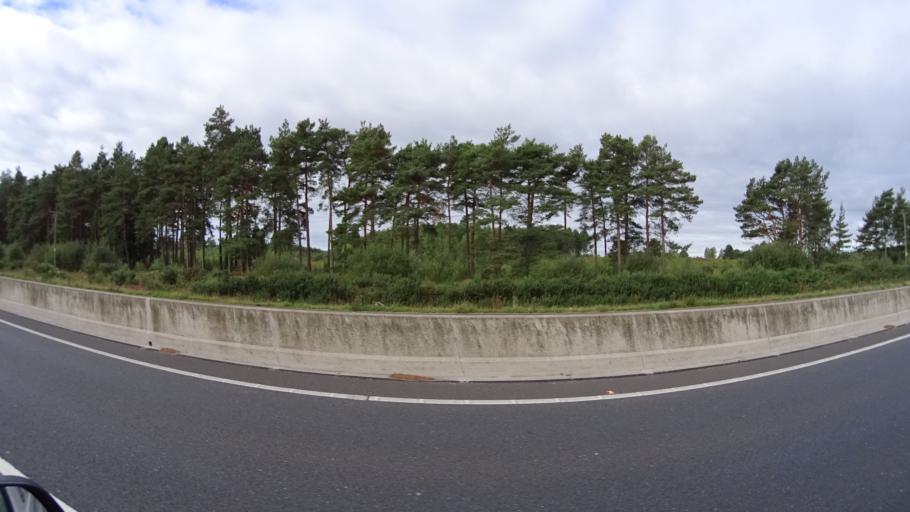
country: GB
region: England
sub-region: Dorset
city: Christchurch
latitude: 50.7820
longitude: -1.8115
